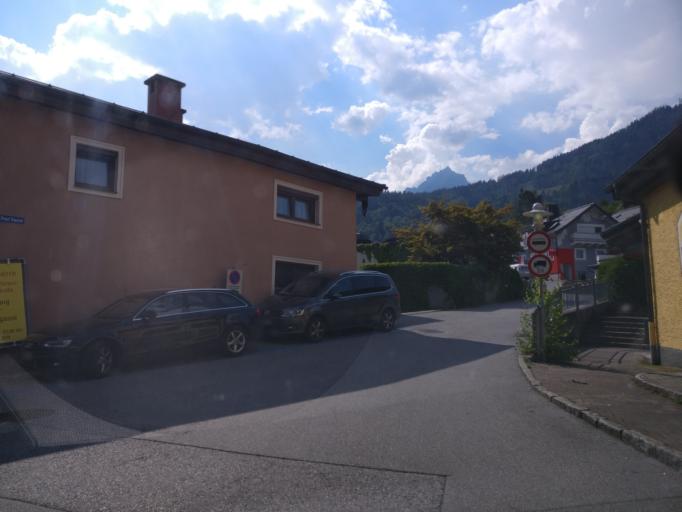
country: AT
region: Salzburg
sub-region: Politischer Bezirk Sankt Johann im Pongau
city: Bischofshofen
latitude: 47.4160
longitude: 13.2174
